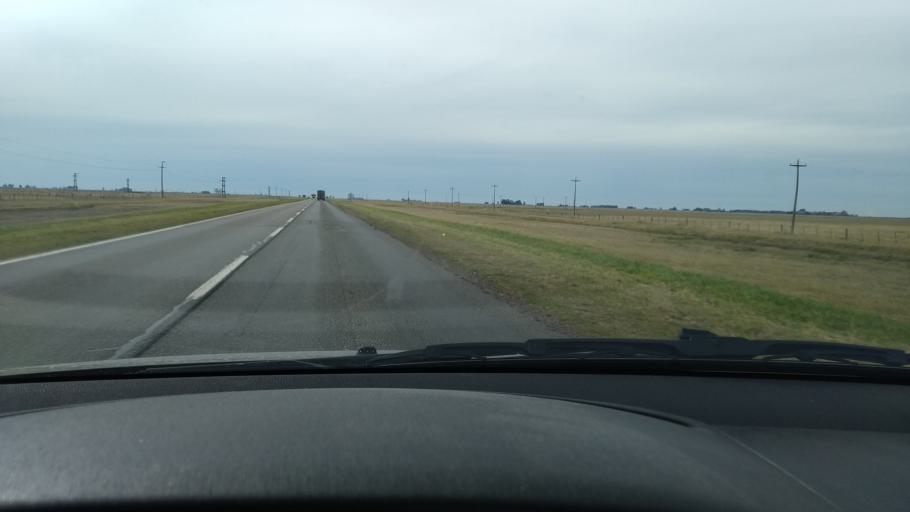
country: AR
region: Buenos Aires
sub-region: Partido de Azul
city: Azul
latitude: -36.7247
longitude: -59.7724
